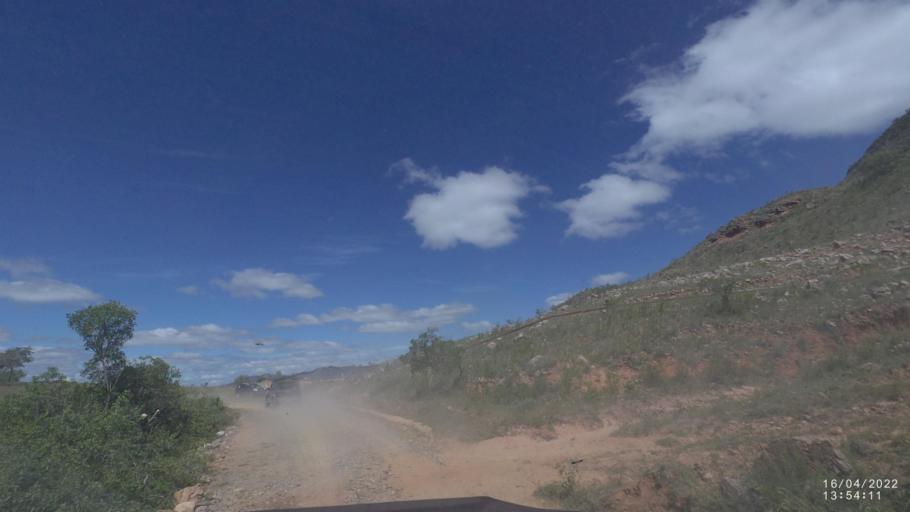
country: BO
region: Cochabamba
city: Mizque
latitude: -18.0261
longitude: -65.5671
